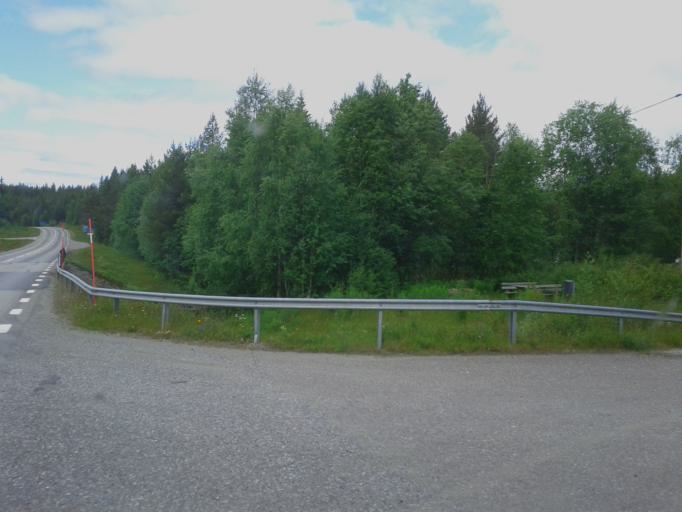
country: SE
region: Vaesterbotten
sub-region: Storumans Kommun
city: Fristad
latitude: 65.3827
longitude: 16.5073
